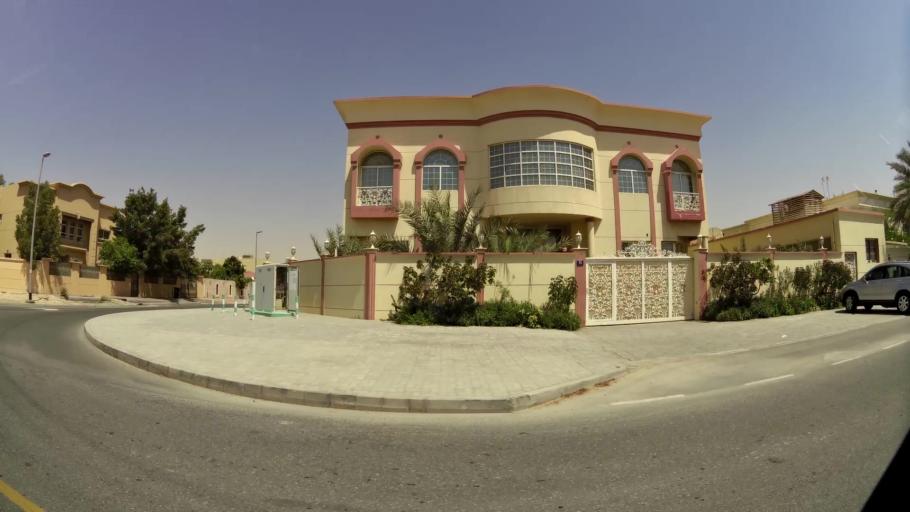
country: AE
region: Dubai
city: Dubai
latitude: 25.1041
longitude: 55.2221
